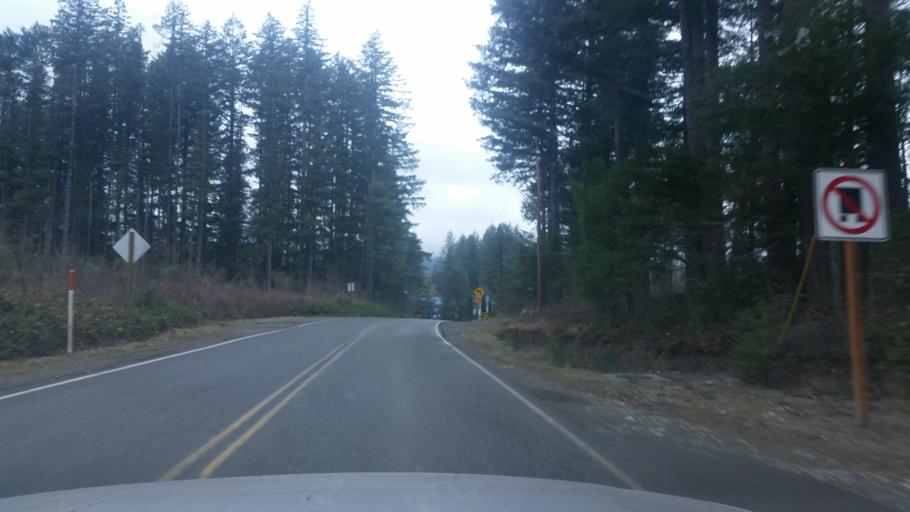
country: US
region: Washington
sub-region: King County
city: Tanner
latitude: 47.4745
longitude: -121.7391
